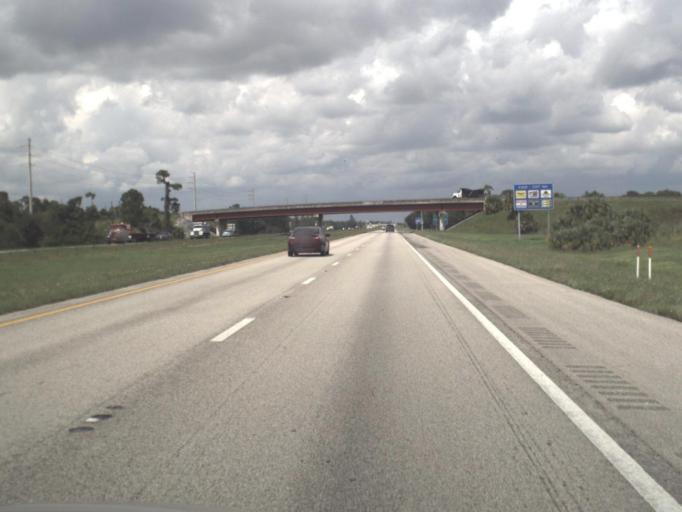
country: US
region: Florida
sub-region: Charlotte County
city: Punta Gorda
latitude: 26.9246
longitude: -82.0142
